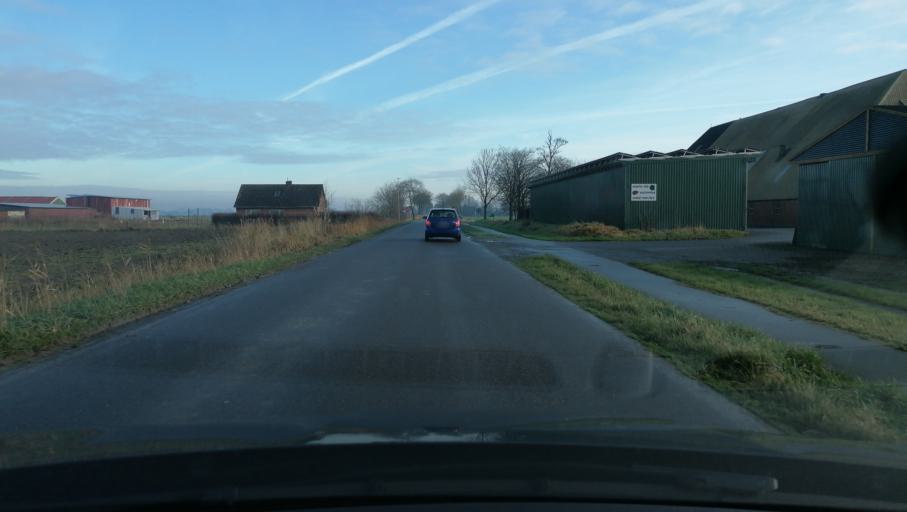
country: DE
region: Schleswig-Holstein
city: Wohrden
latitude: 54.1217
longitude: 8.9914
